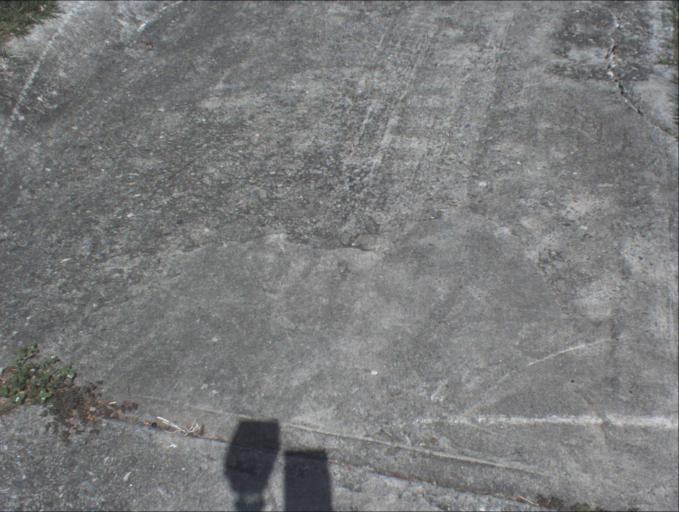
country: AU
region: Queensland
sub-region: Logan
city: Slacks Creek
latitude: -27.6441
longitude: 153.1592
